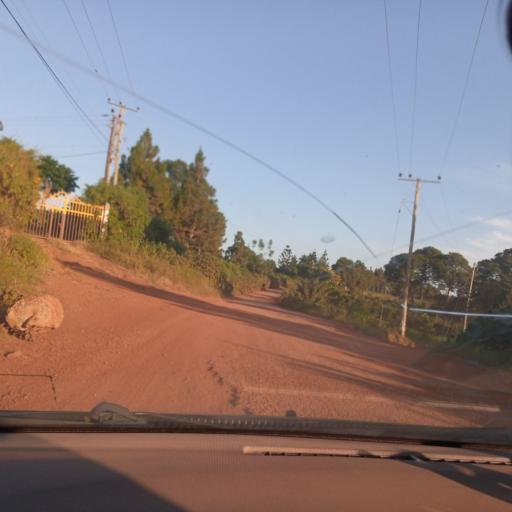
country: UG
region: Central Region
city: Masaka
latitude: -0.3367
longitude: 31.7622
